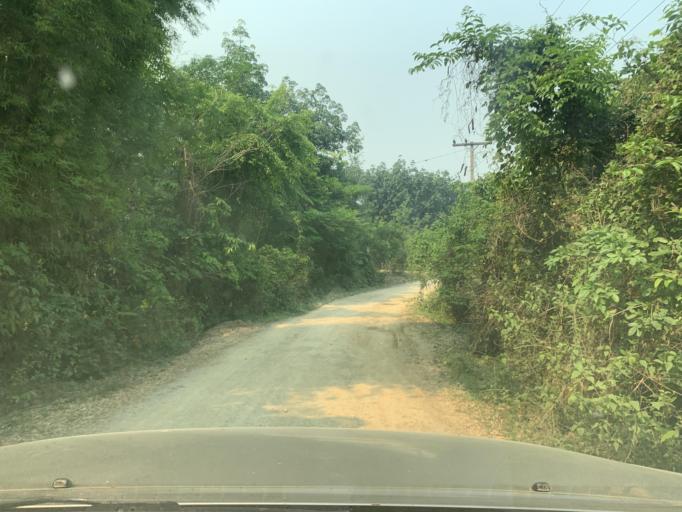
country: LA
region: Louangphabang
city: Louangphabang
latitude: 19.8916
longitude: 102.2509
